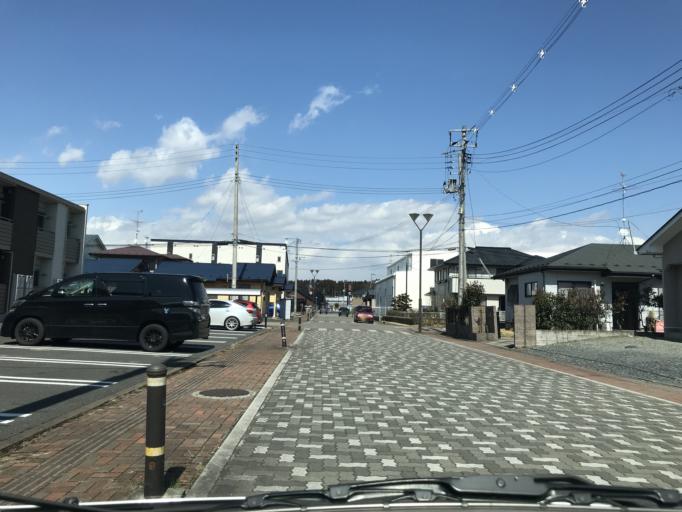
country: JP
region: Miyagi
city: Wakuya
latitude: 38.6877
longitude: 141.1814
